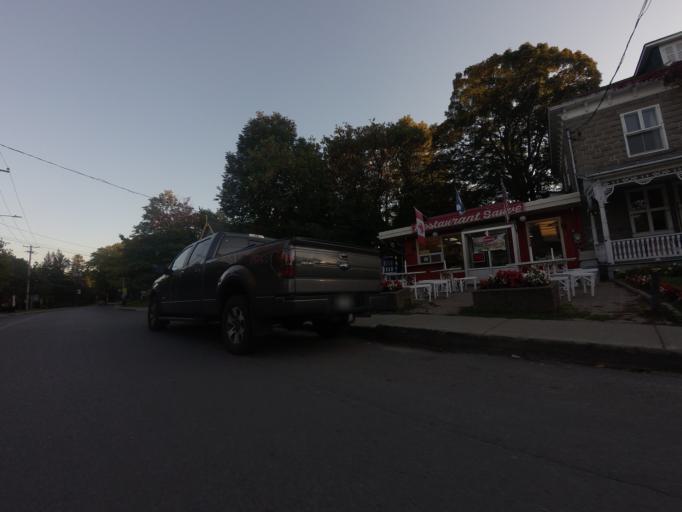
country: CA
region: Quebec
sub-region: Monteregie
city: Hudson
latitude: 45.4571
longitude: -74.1385
